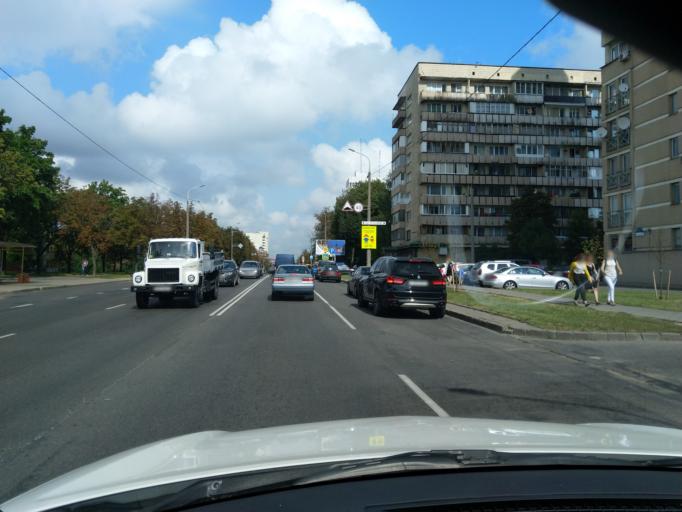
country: BY
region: Minsk
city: Minsk
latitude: 53.8979
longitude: 27.5871
